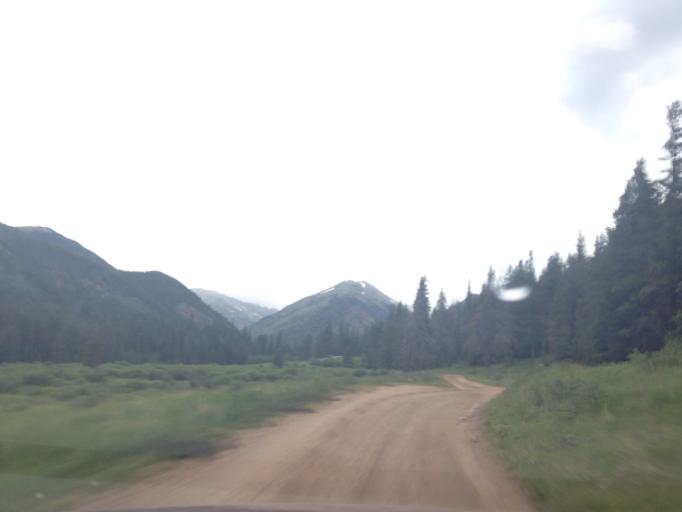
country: US
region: Colorado
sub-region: Clear Creek County
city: Georgetown
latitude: 39.5460
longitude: -105.7478
